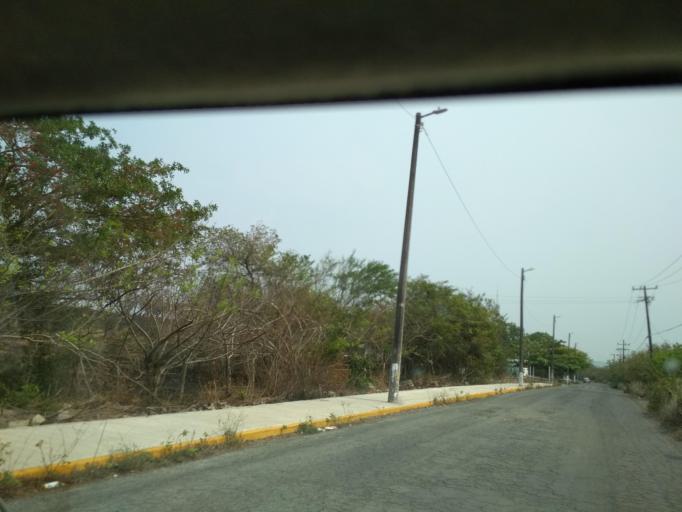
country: MX
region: Veracruz
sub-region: Veracruz
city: Delfino Victoria (Santa Fe)
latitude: 19.1982
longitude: -96.2756
